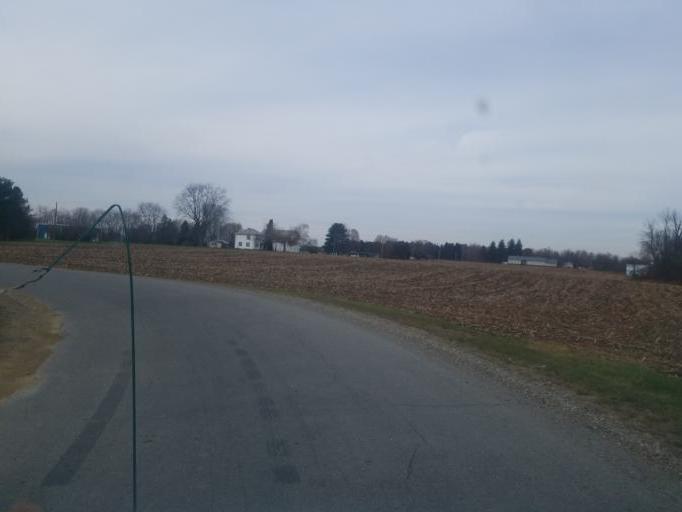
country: US
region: Ohio
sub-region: Knox County
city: Mount Vernon
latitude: 40.4128
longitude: -82.5121
